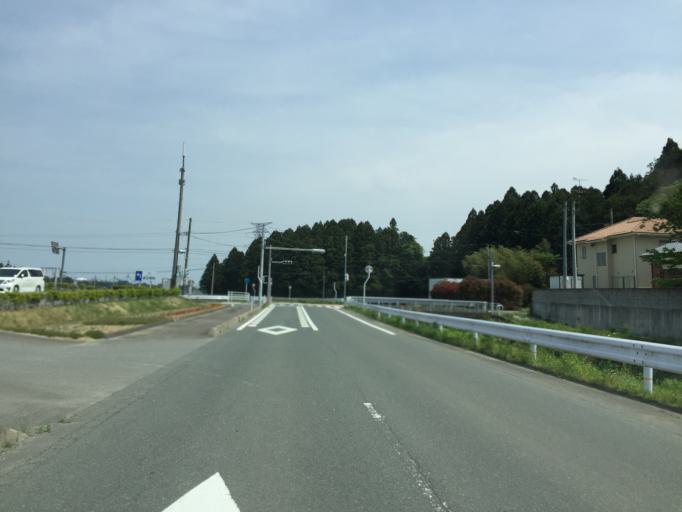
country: JP
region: Miyagi
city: Marumori
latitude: 37.8479
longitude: 140.8948
